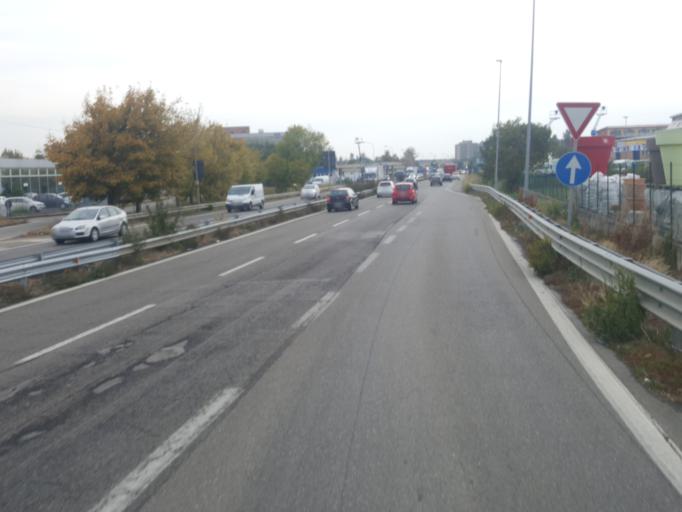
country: IT
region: Emilia-Romagna
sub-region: Provincia di Modena
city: Modena
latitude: 44.6503
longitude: 10.9624
